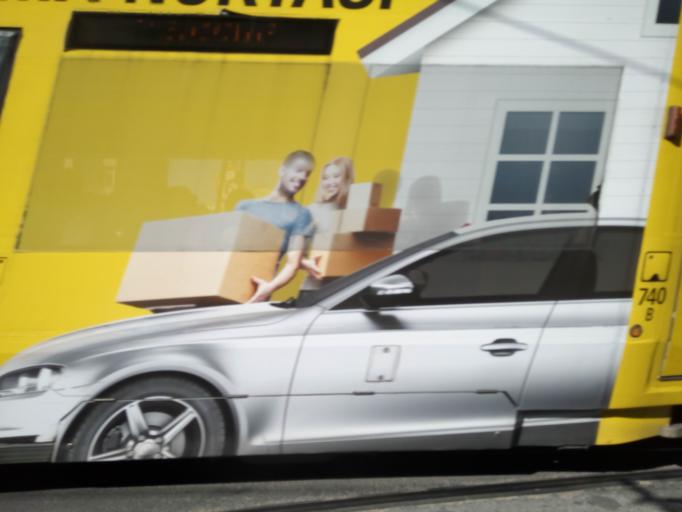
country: TR
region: Istanbul
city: Istanbul
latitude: 41.0166
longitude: 28.9309
